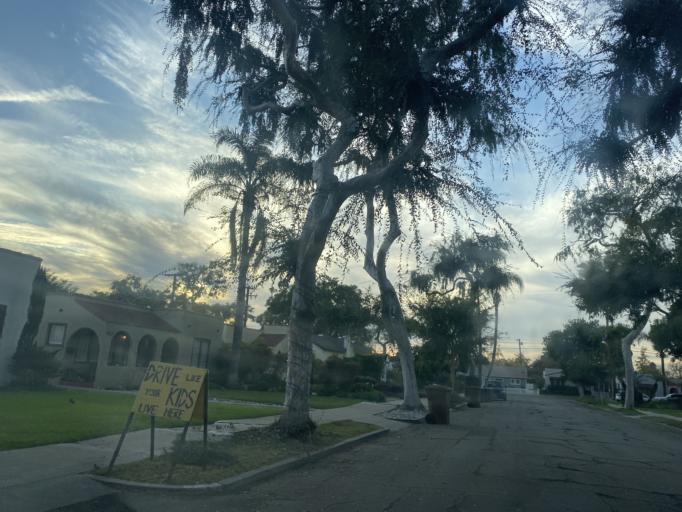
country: US
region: California
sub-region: Orange County
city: Fullerton
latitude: 33.8732
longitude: -117.9078
